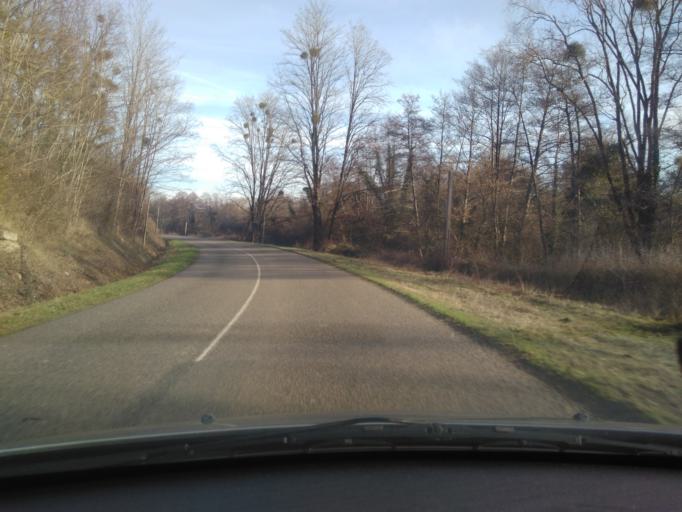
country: FR
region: Bourgogne
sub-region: Departement de la Nievre
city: Saint-Parize-le-Chatel
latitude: 46.8116
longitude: 3.2516
